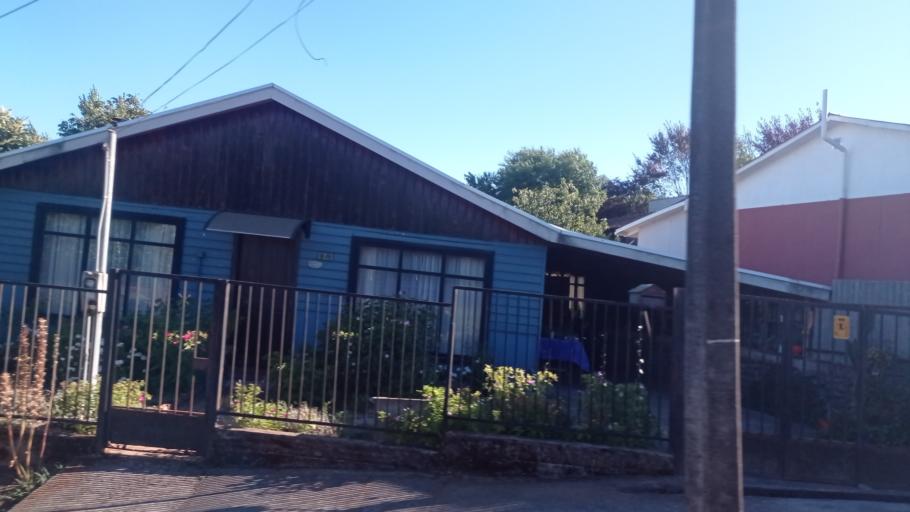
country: CL
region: Biobio
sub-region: Provincia de Biobio
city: Nacimiento
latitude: -37.5003
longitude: -72.6775
